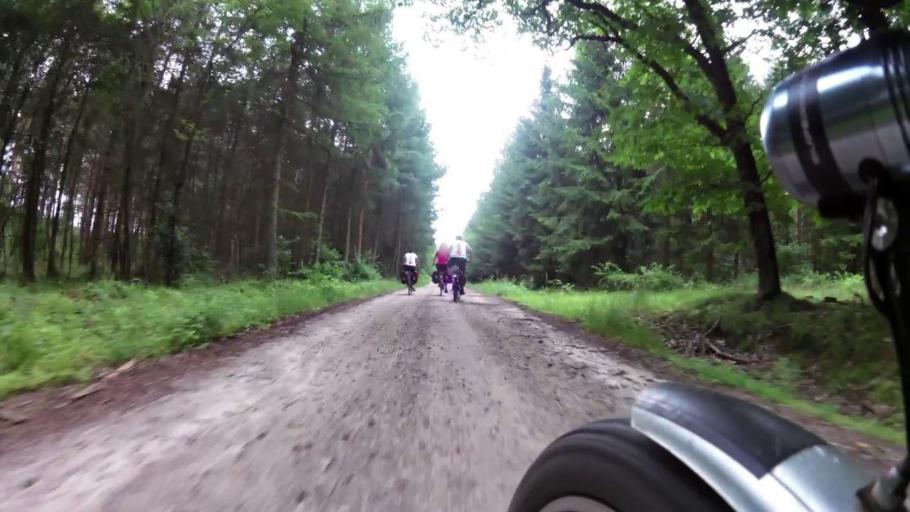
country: PL
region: West Pomeranian Voivodeship
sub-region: Powiat gryfinski
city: Mieszkowice
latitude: 52.8378
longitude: 14.5947
